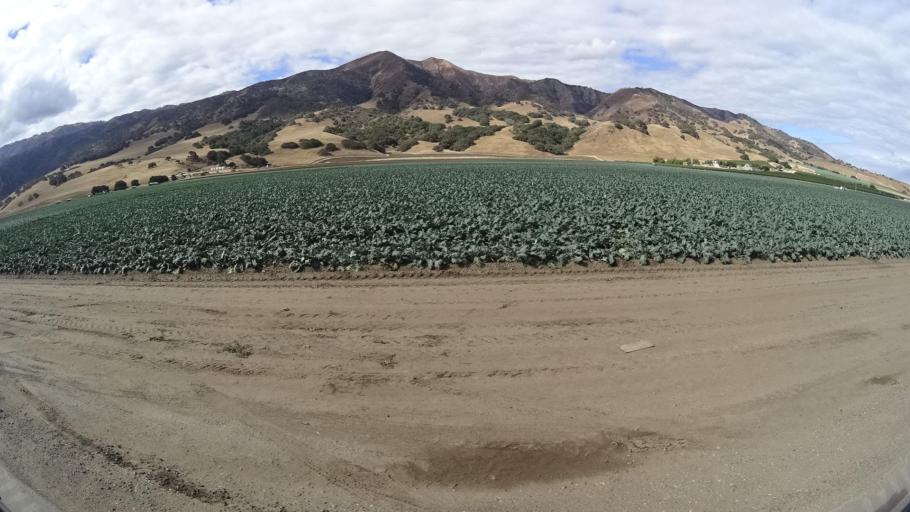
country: US
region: California
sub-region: Monterey County
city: Chualar
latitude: 36.5442
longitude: -121.5434
